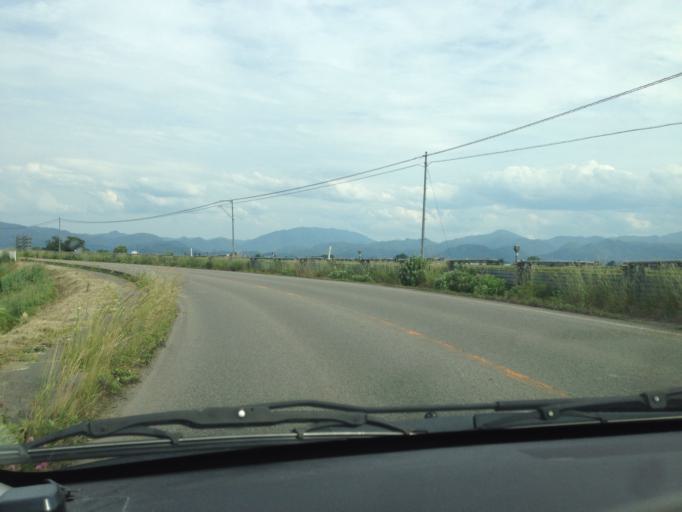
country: JP
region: Fukushima
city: Kitakata
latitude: 37.5012
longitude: 139.8326
